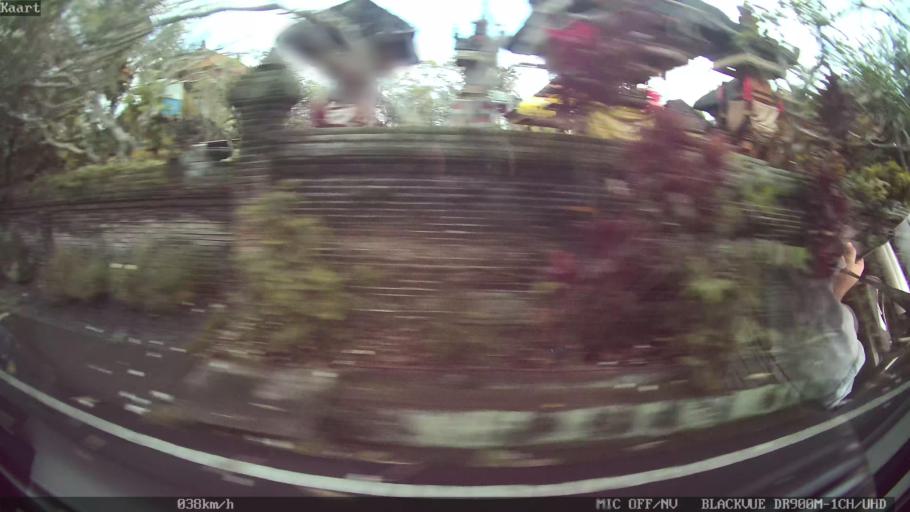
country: ID
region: Bali
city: Banjar Mambalkajanan
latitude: -8.5579
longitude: 115.2085
